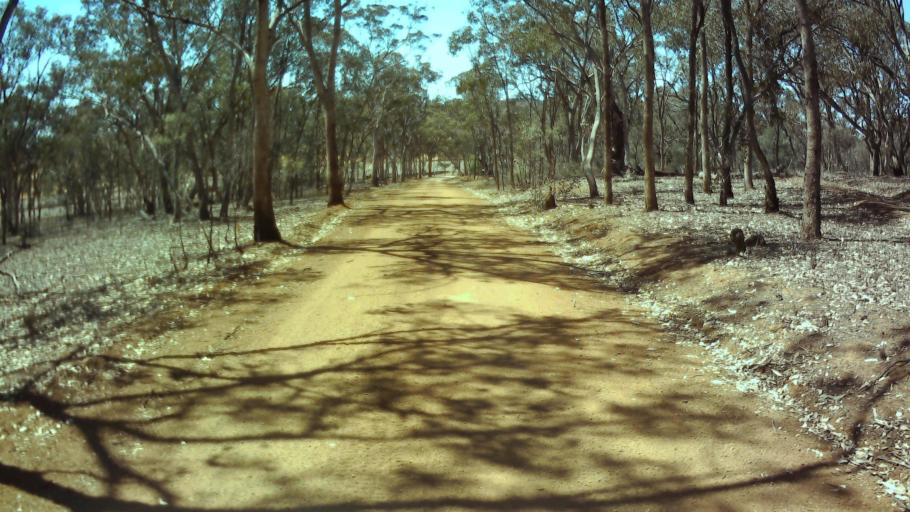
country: AU
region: New South Wales
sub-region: Weddin
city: Grenfell
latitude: -33.9468
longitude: 148.0820
